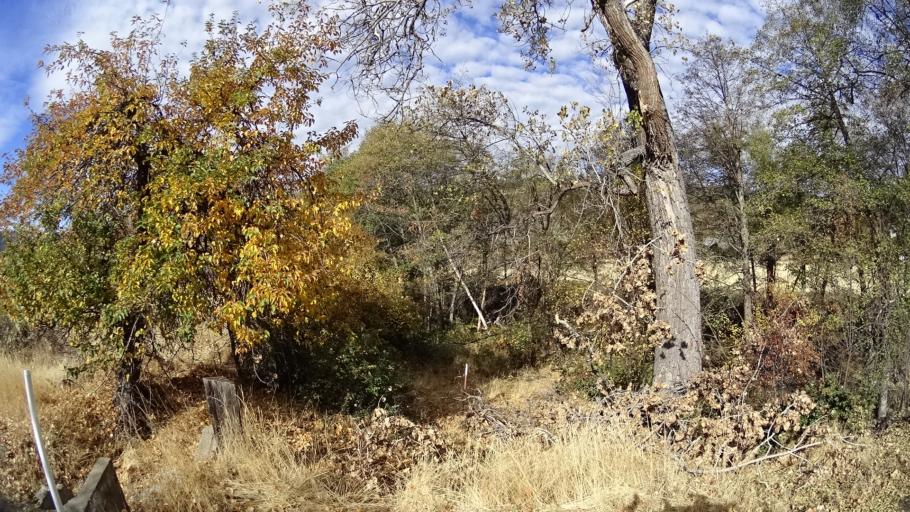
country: US
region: California
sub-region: Siskiyou County
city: Yreka
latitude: 41.6338
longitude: -122.7492
